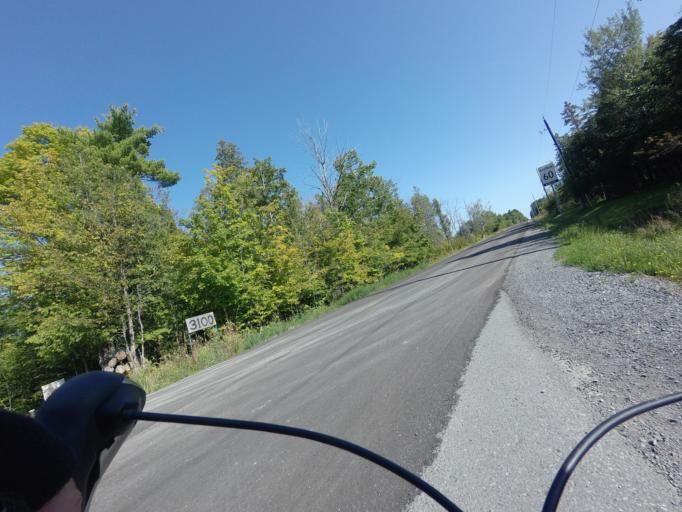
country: CA
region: Ontario
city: Bells Corners
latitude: 45.4672
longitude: -75.9854
